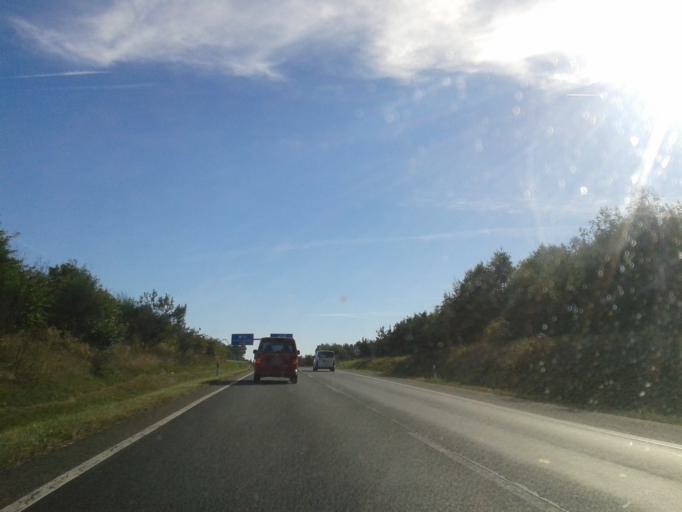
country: DE
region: Saxony
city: Albertstadt
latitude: 51.1353
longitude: 13.7506
